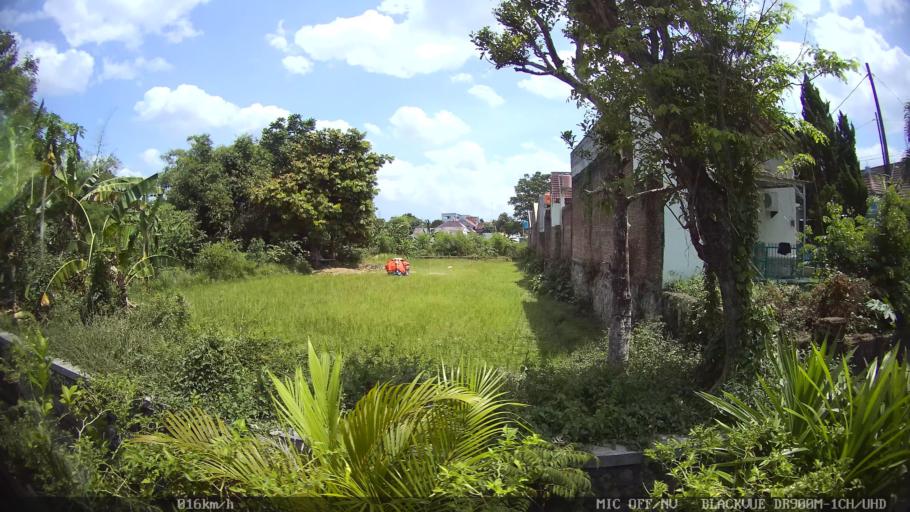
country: ID
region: Daerah Istimewa Yogyakarta
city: Kasihan
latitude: -7.8234
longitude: 110.3533
